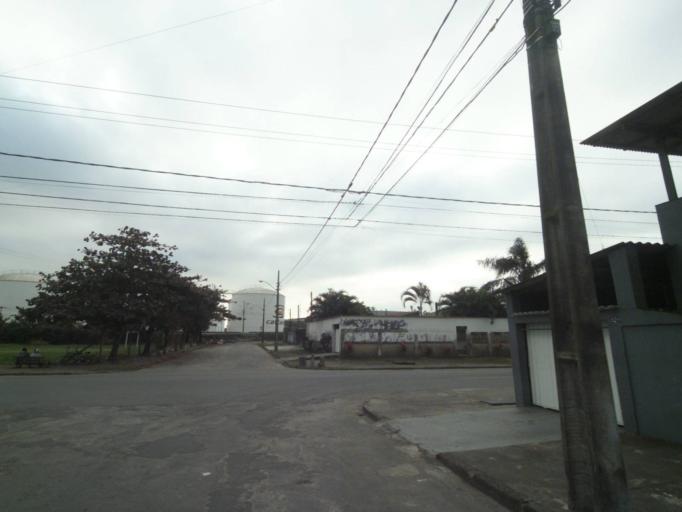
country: BR
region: Parana
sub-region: Paranagua
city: Paranagua
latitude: -25.5195
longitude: -48.5238
